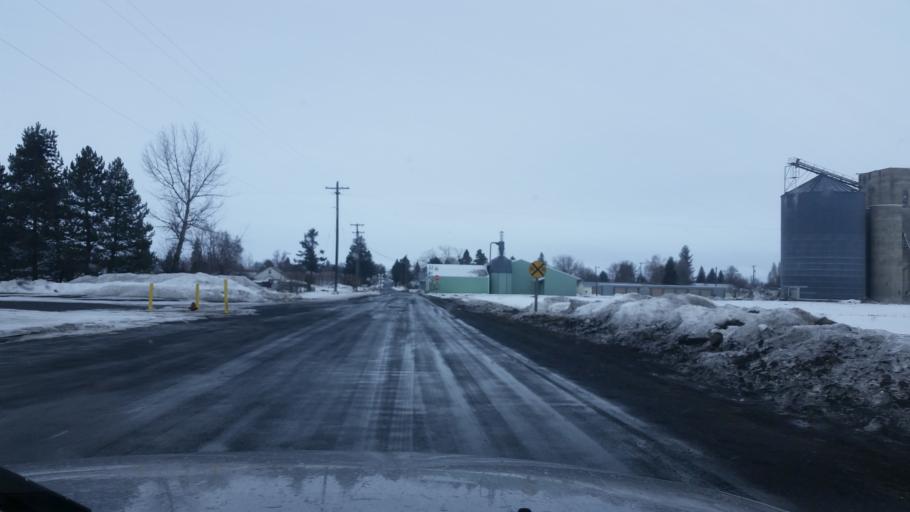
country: US
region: Washington
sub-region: Lincoln County
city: Davenport
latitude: 47.6458
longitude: -118.1472
